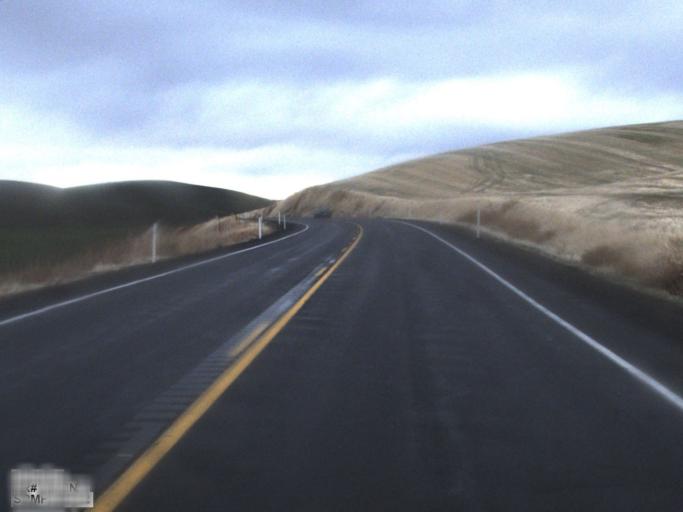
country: US
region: Washington
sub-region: Walla Walla County
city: Waitsburg
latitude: 46.1930
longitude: -118.1376
